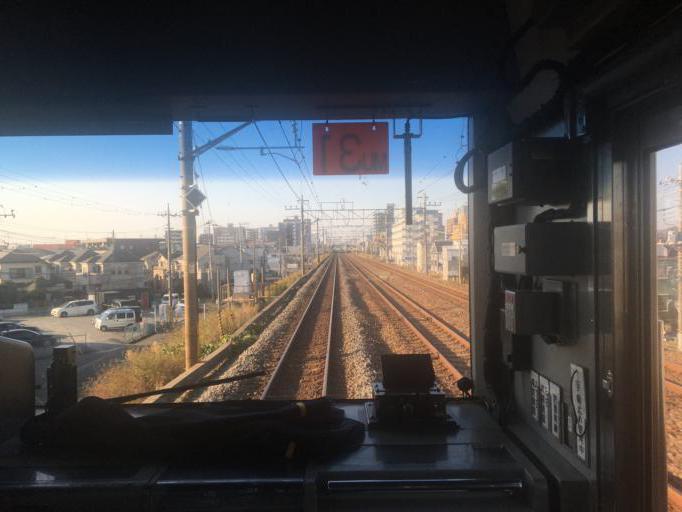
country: JP
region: Chiba
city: Nagareyama
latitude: 35.8344
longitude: 139.9073
